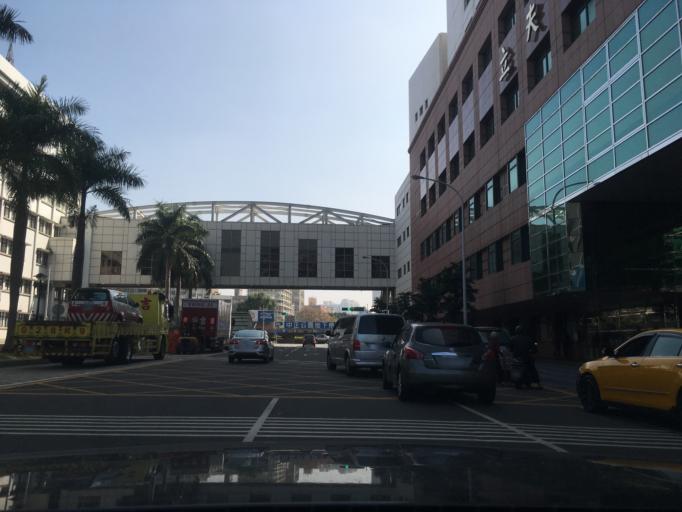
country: TW
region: Taiwan
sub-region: Taichung City
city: Taichung
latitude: 24.1573
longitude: 120.6801
